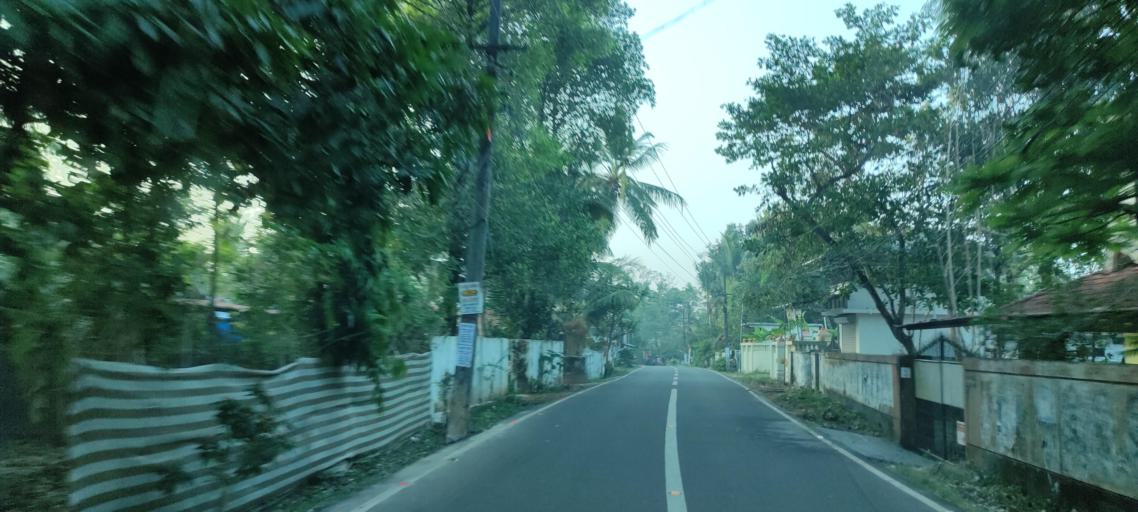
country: IN
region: Kerala
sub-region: Alappuzha
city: Alleppey
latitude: 9.4468
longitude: 76.3461
